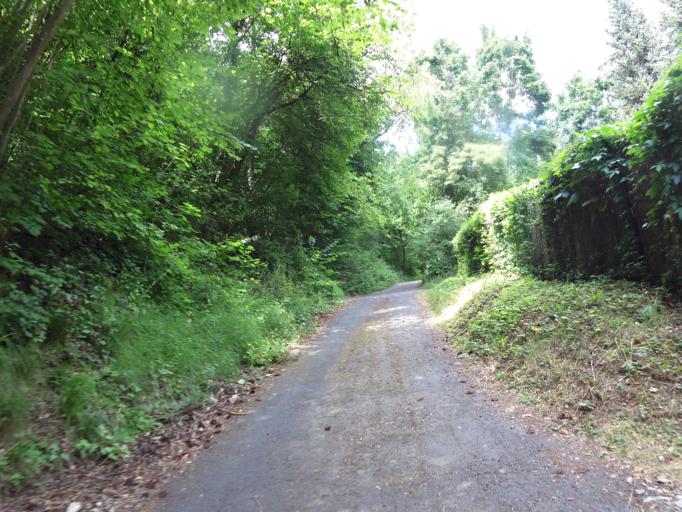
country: DE
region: Bavaria
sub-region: Regierungsbezirk Unterfranken
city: Veitshochheim
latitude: 49.8121
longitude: 9.9067
